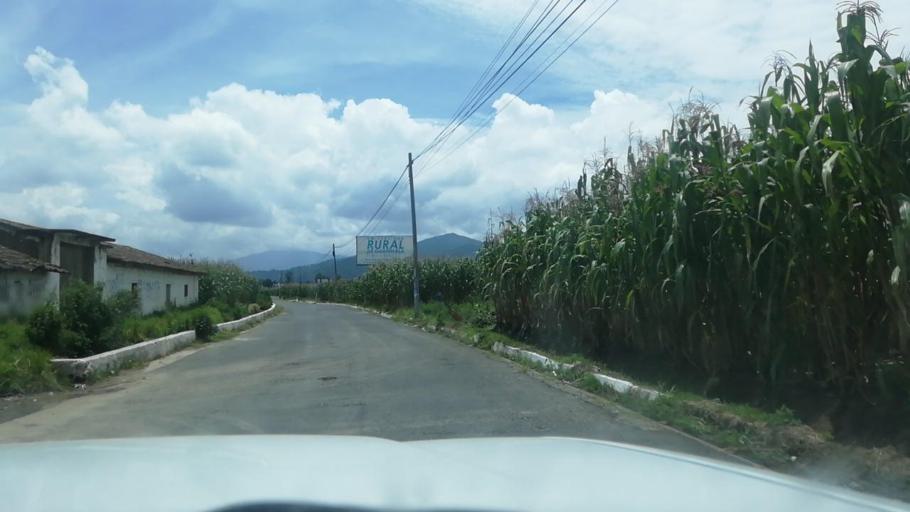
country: GT
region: Totonicapan
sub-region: Municipio de San Andres Xecul
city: San Andres Xecul
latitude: 14.9050
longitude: -91.4728
